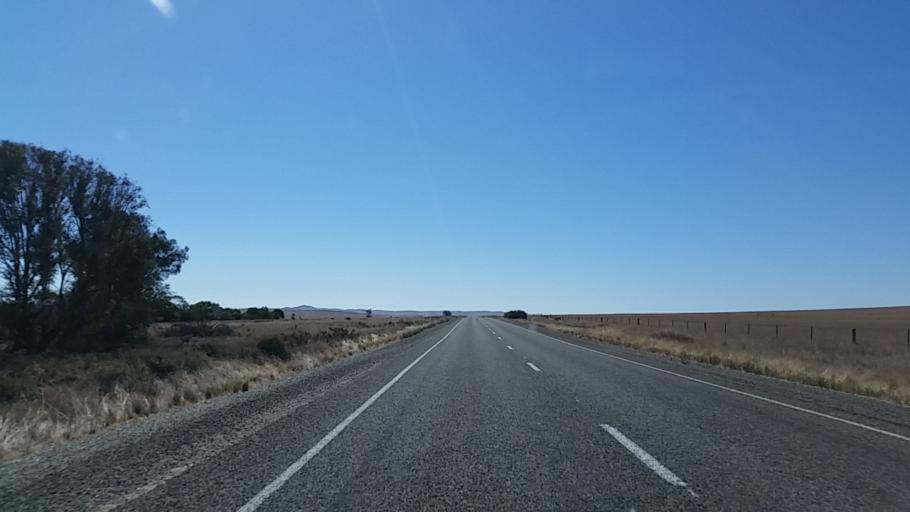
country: AU
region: South Australia
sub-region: Northern Areas
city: Jamestown
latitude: -33.2972
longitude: 138.8737
